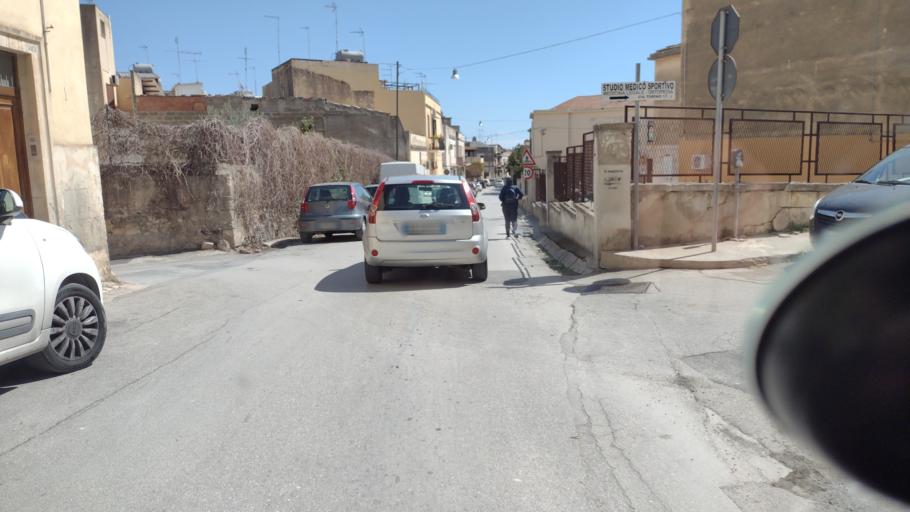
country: IT
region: Sicily
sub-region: Provincia di Siracusa
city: Noto
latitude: 36.8888
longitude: 15.0697
